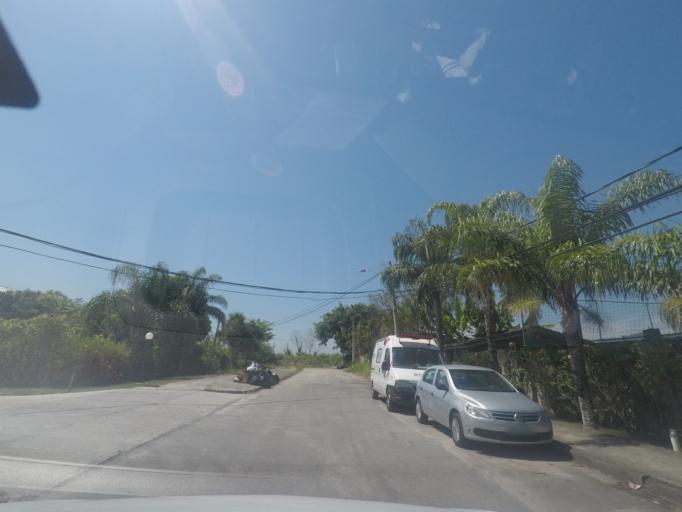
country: BR
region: Rio de Janeiro
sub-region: Nilopolis
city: Nilopolis
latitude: -22.9913
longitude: -43.4797
